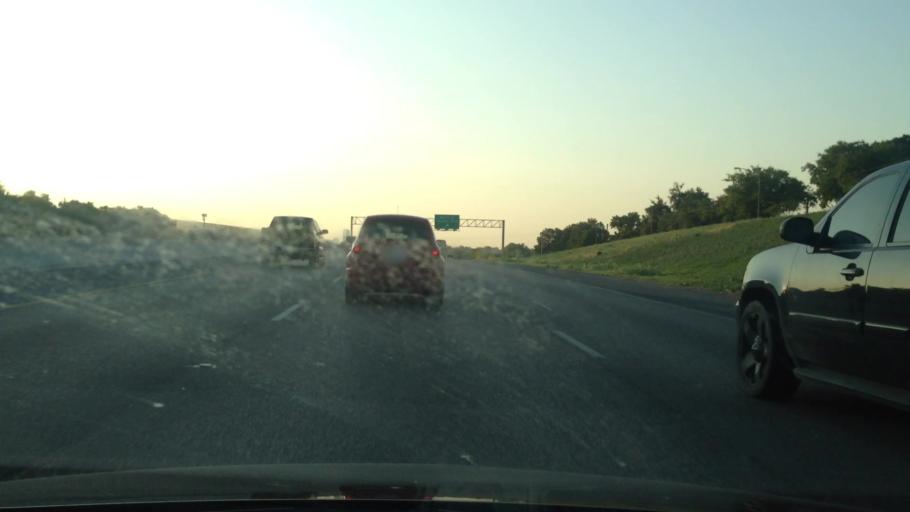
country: US
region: Texas
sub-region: Tarrant County
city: Forest Hill
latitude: 32.7088
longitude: -97.2728
